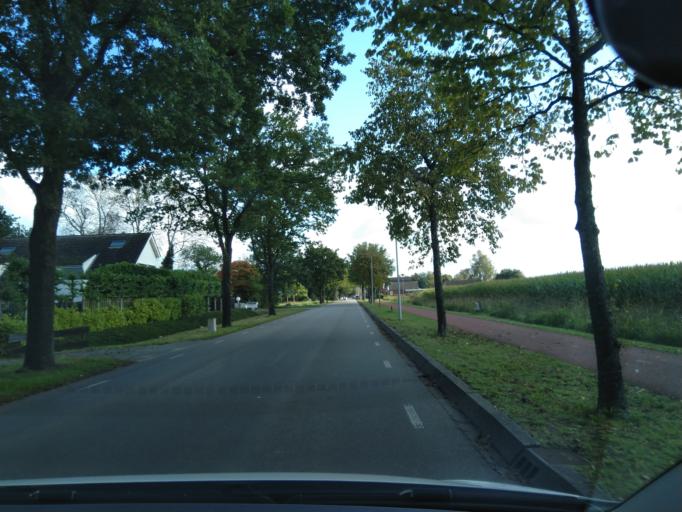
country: NL
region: Groningen
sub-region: Gemeente Veendam
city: Veendam
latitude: 53.0955
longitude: 6.9164
